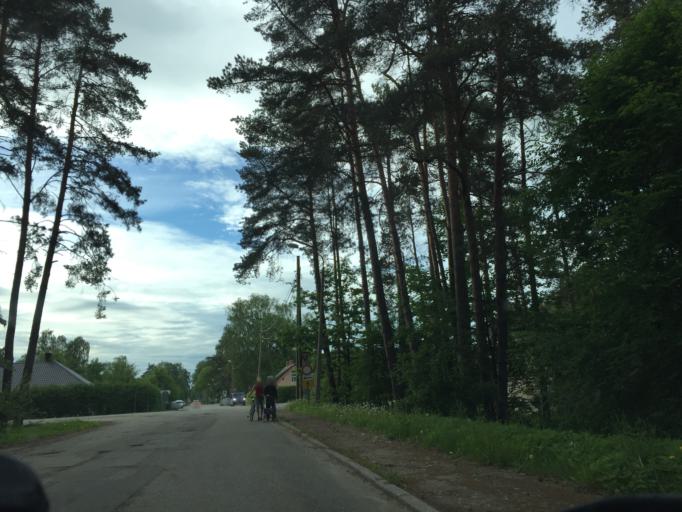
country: LV
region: Valmieras Rajons
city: Valmiera
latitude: 57.5242
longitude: 25.4301
